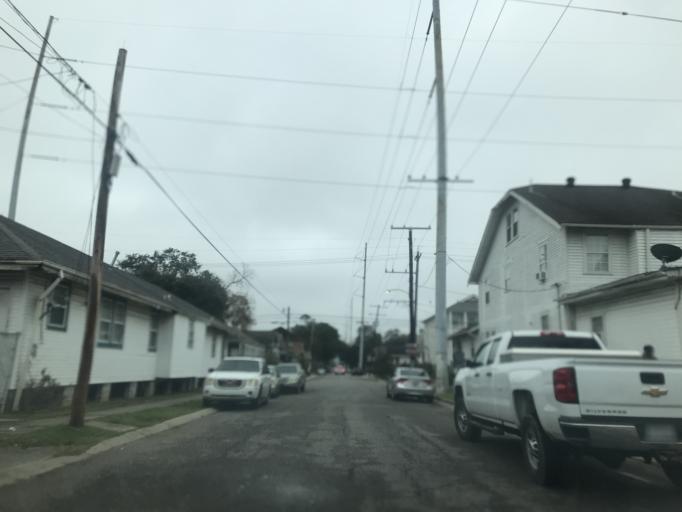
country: US
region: Louisiana
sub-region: Orleans Parish
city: New Orleans
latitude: 29.9682
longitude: -90.0996
